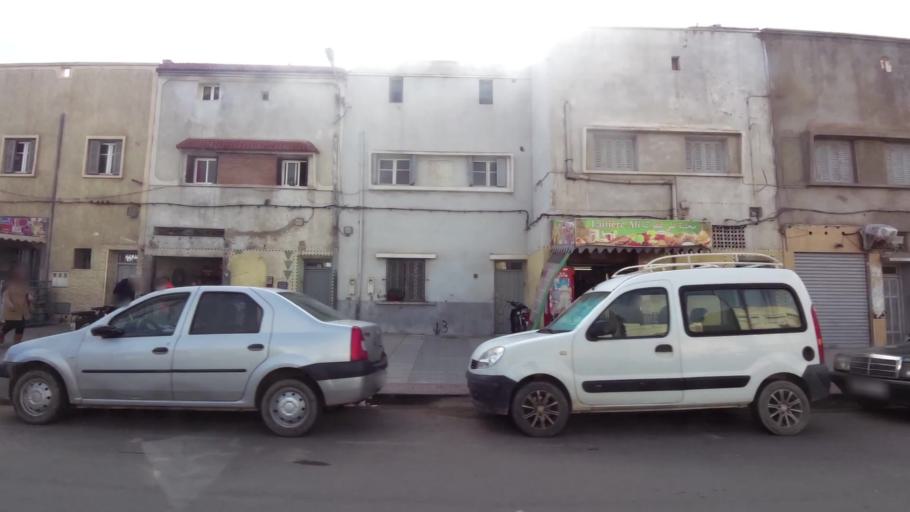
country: MA
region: Doukkala-Abda
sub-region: El-Jadida
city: El Jadida
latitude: 33.2488
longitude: -8.5177
